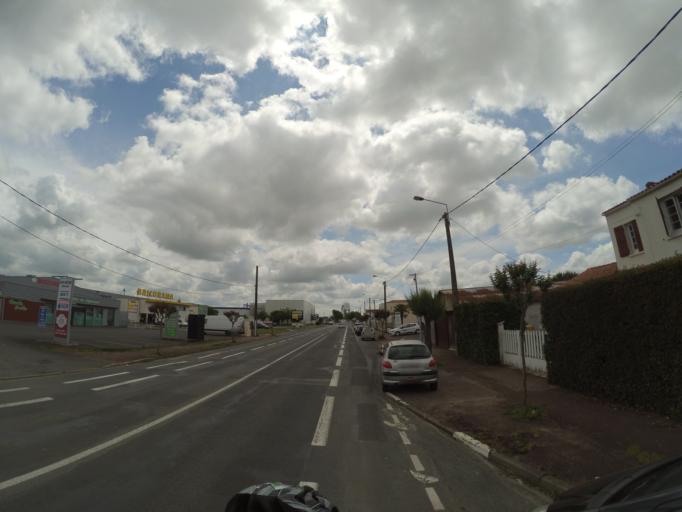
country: FR
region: Poitou-Charentes
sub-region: Departement de la Charente-Maritime
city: Rochefort
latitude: 45.9268
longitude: -0.9601
